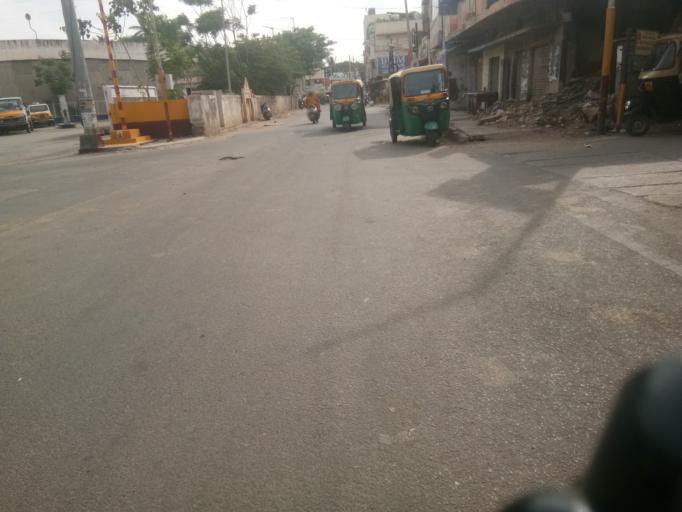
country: IN
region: Karnataka
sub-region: Bangalore Urban
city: Bangalore
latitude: 13.0050
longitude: 77.6372
